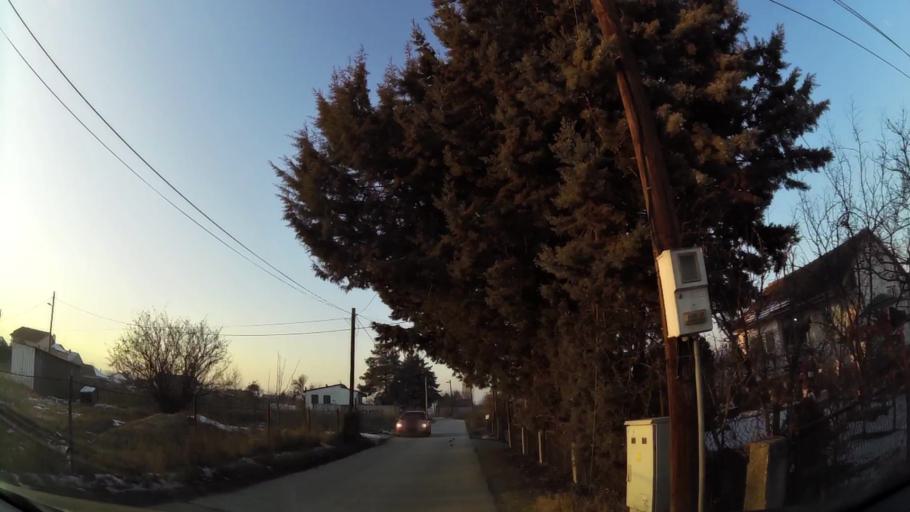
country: MK
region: Kisela Voda
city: Kisela Voda
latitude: 41.9800
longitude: 21.4945
